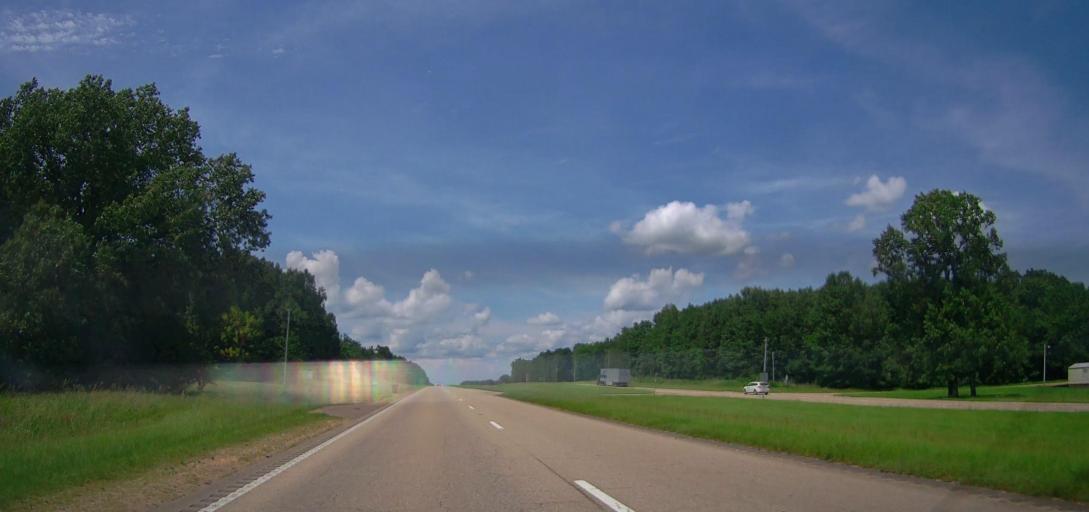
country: US
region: Mississippi
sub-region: Lee County
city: Nettleton
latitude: 34.0106
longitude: -88.6326
